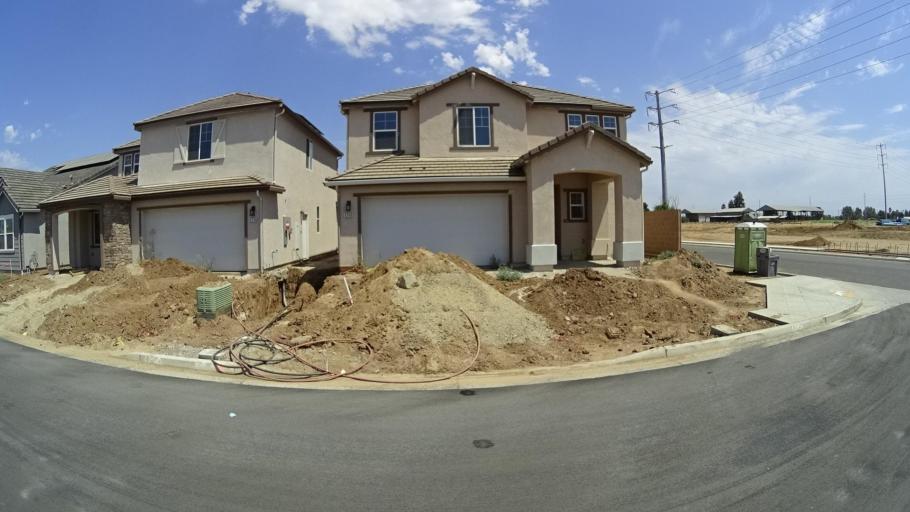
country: US
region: California
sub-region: Fresno County
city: Sunnyside
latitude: 36.7697
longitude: -119.6780
